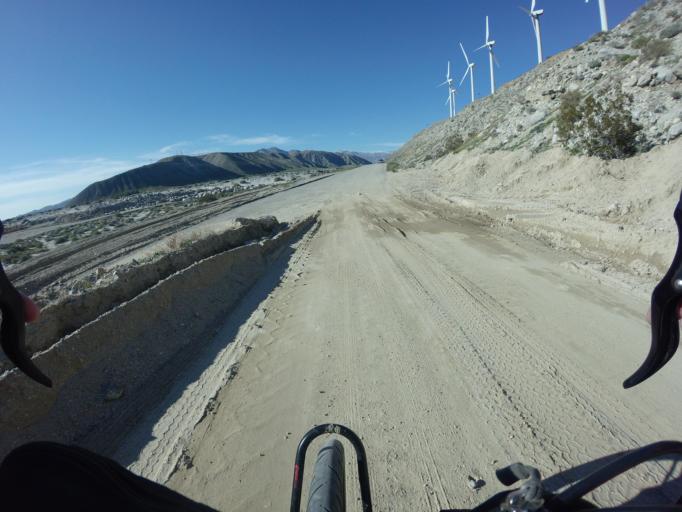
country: US
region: California
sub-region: Riverside County
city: Garnet
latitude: 33.9228
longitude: -116.6318
